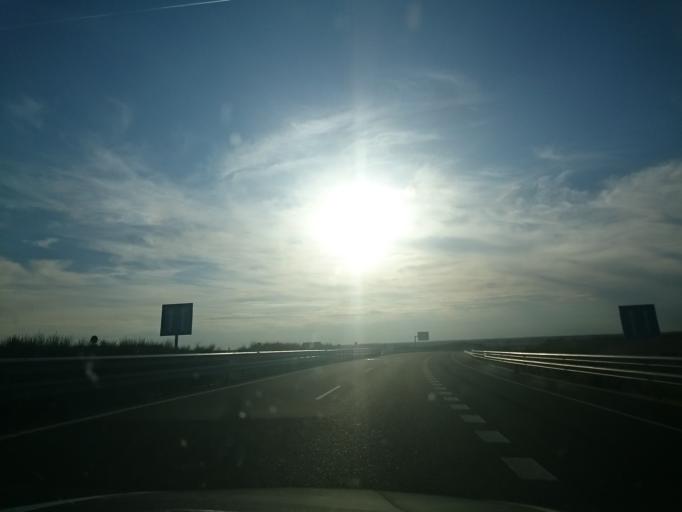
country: ES
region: Castille and Leon
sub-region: Provincia de Leon
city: Sahagun
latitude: 42.3666
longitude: -4.9797
